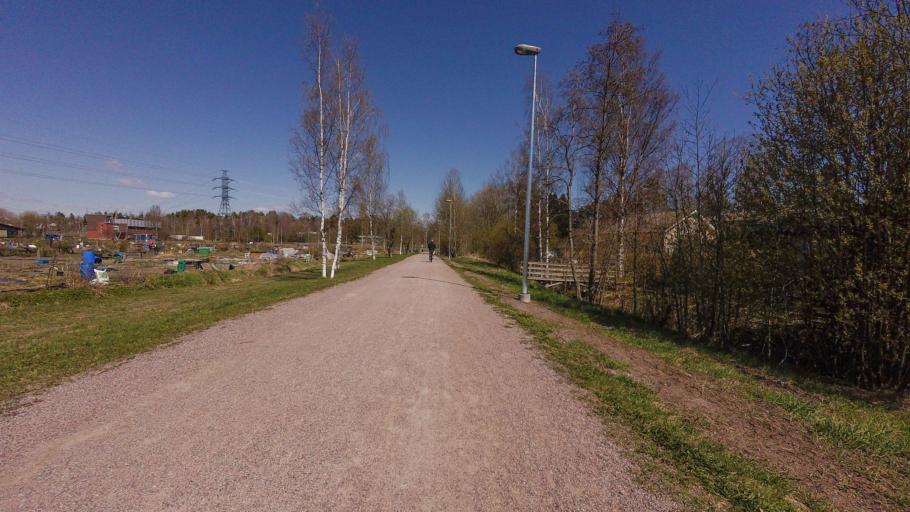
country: FI
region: Uusimaa
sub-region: Helsinki
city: Vantaa
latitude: 60.2303
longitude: 25.1104
